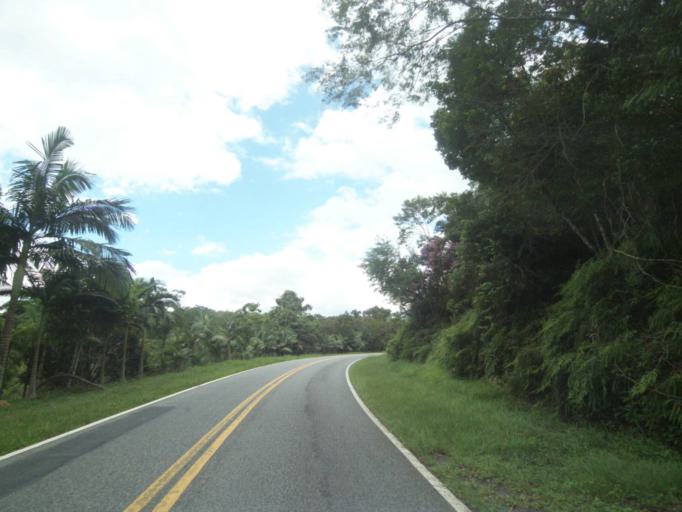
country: BR
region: Parana
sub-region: Antonina
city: Antonina
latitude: -25.5249
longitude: -48.7920
